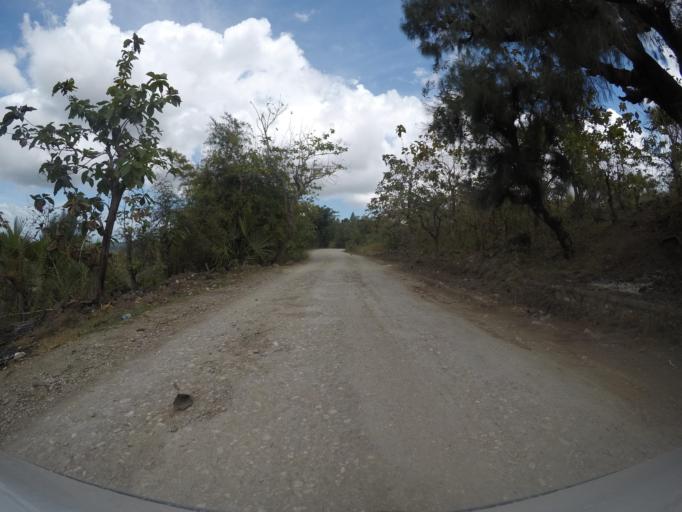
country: TL
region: Viqueque
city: Viqueque
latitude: -8.8854
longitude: 126.3853
